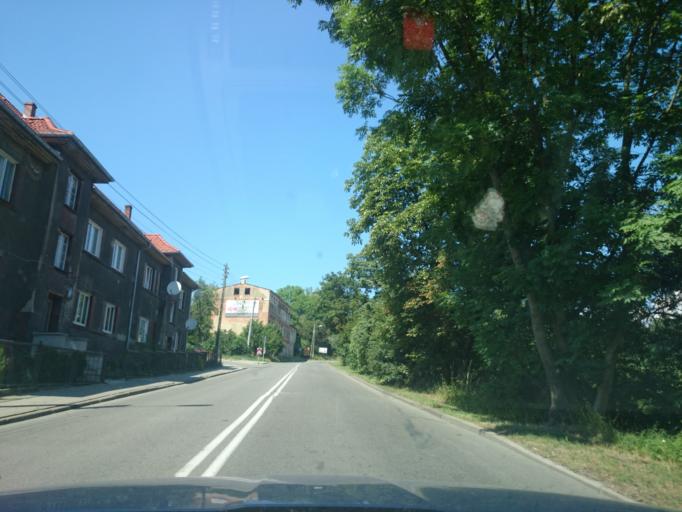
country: PL
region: West Pomeranian Voivodeship
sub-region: Powiat policki
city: Police
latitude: 53.4859
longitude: 14.6113
